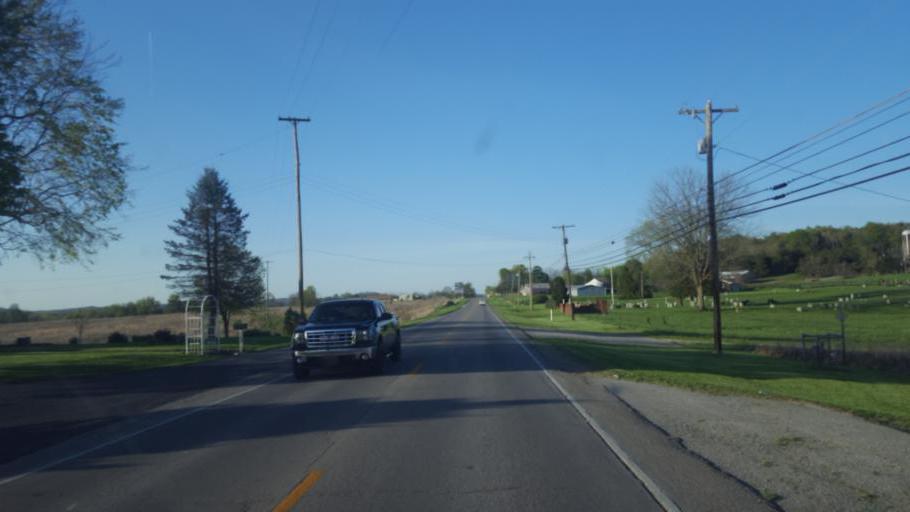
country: US
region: Kentucky
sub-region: Hart County
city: Munfordville
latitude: 37.2462
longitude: -85.8910
